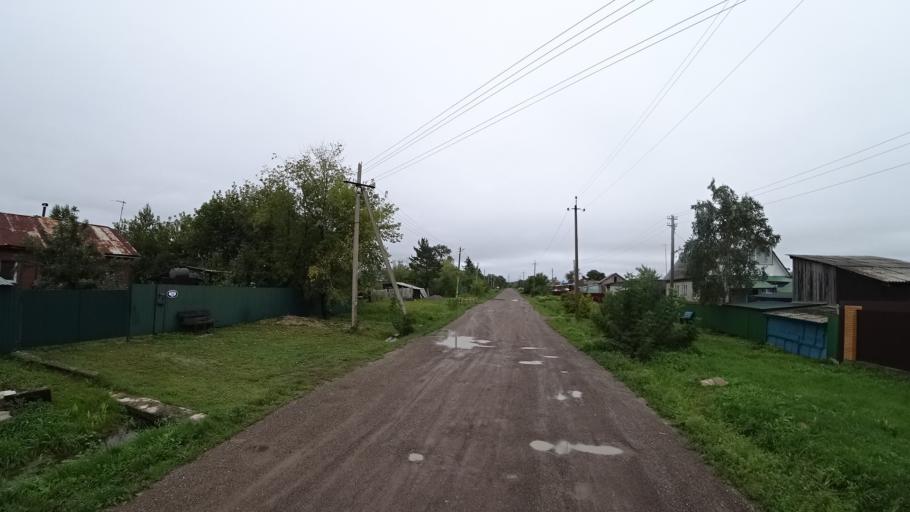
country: RU
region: Primorskiy
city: Monastyrishche
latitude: 44.1982
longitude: 132.4561
